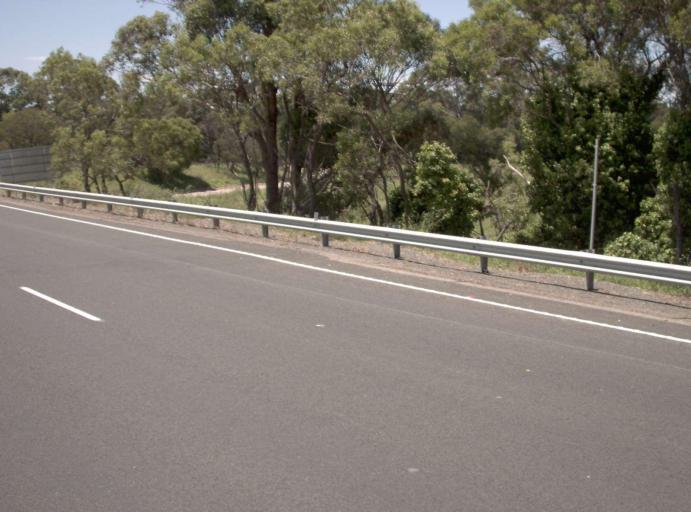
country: AU
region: Victoria
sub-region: East Gippsland
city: Lakes Entrance
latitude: -37.7182
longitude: 148.4526
